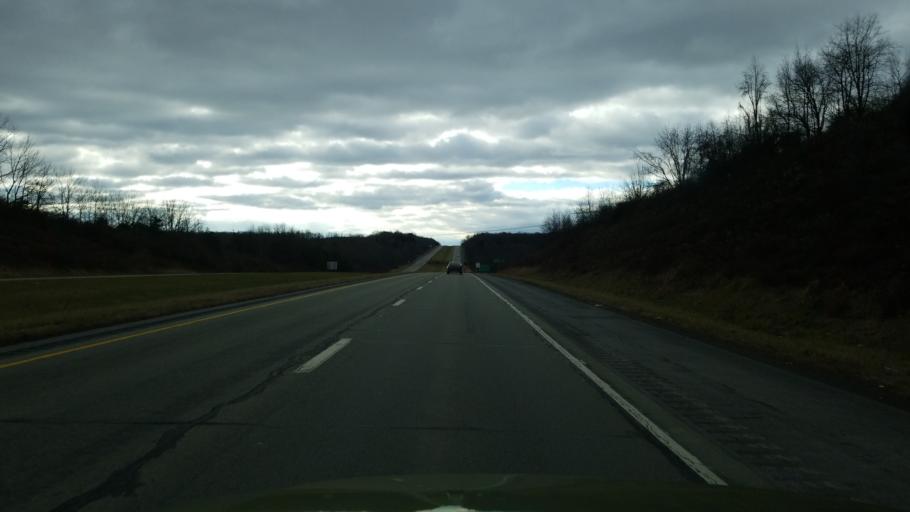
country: US
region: Pennsylvania
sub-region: Indiana County
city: Chevy Chase Heights
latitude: 40.6618
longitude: -79.1145
